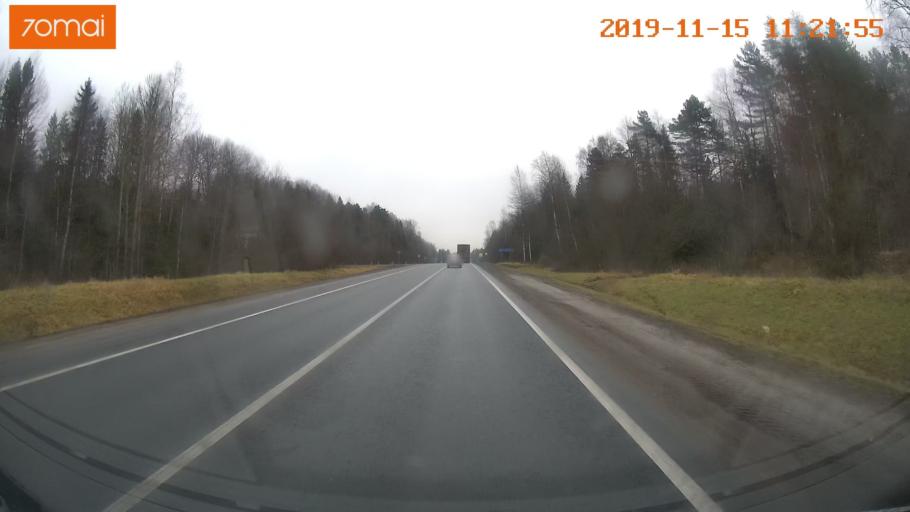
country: RU
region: Vologda
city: Molochnoye
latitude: 59.1461
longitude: 39.3498
